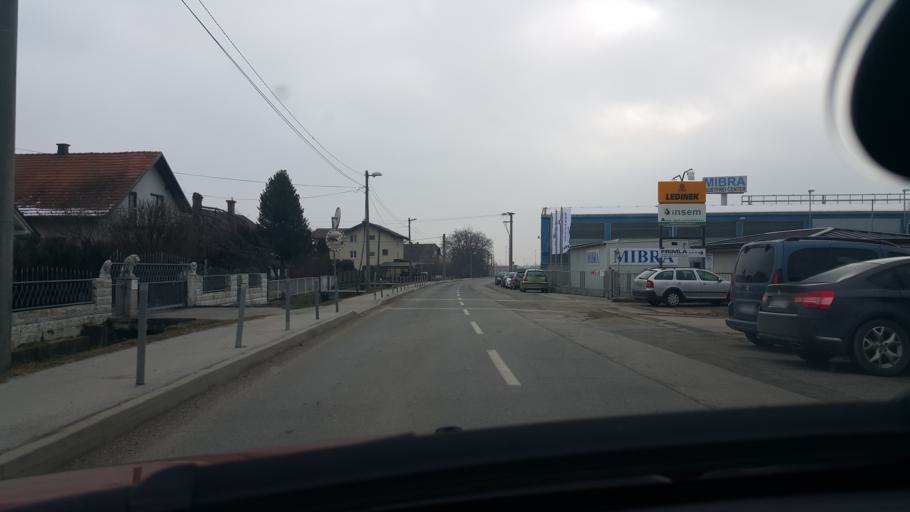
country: SI
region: Hoce-Slivnica
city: Spodnje Hoce
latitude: 46.4984
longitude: 15.6497
